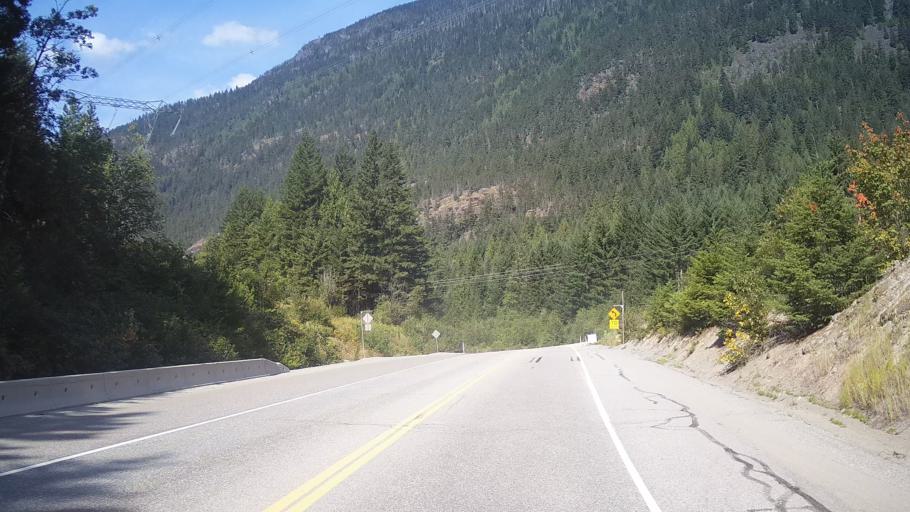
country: CA
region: British Columbia
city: Pemberton
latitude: 50.2870
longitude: -122.8433
